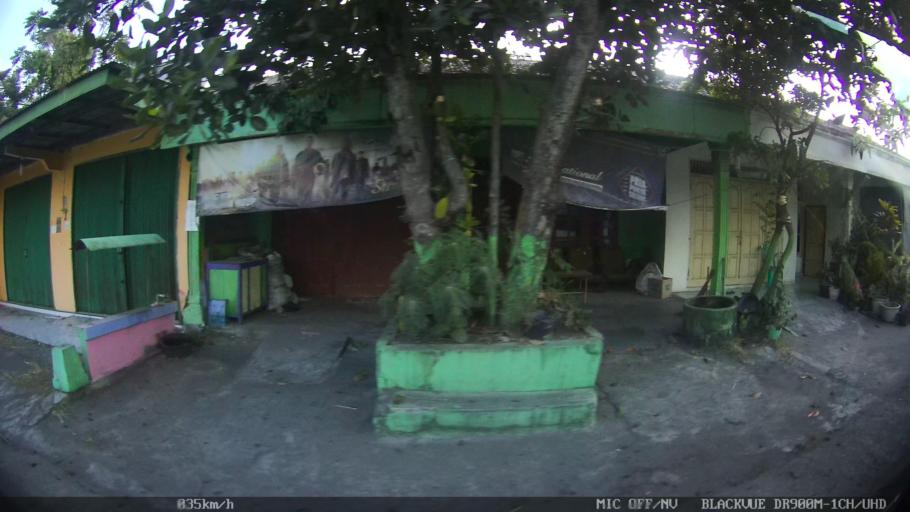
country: ID
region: Central Java
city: Candi Prambanan
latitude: -7.7152
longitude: 110.4717
